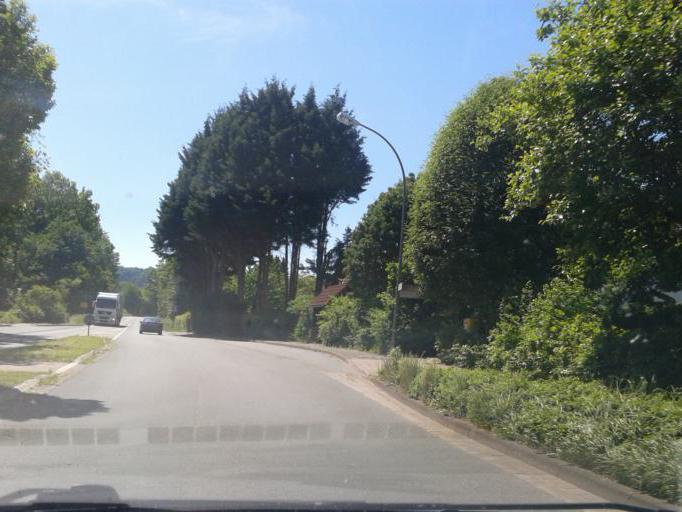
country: DE
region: North Rhine-Westphalia
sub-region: Regierungsbezirk Detmold
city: Bad Meinberg
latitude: 51.9193
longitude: 9.0312
